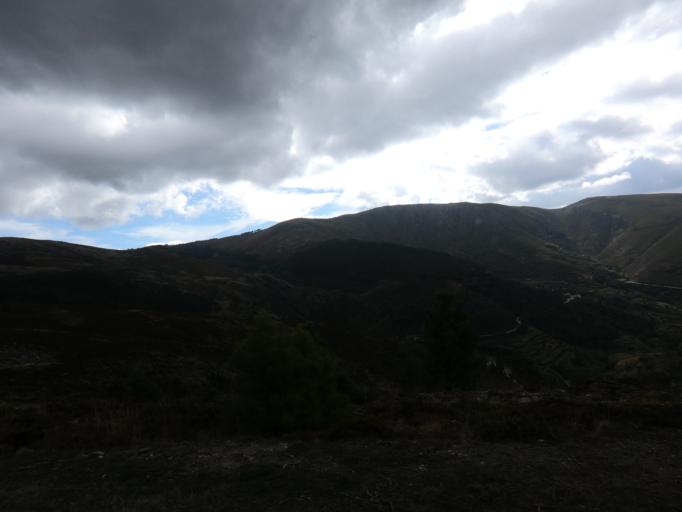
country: PT
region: Vila Real
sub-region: Vila Real
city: Vila Real
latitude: 41.3706
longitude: -7.8397
